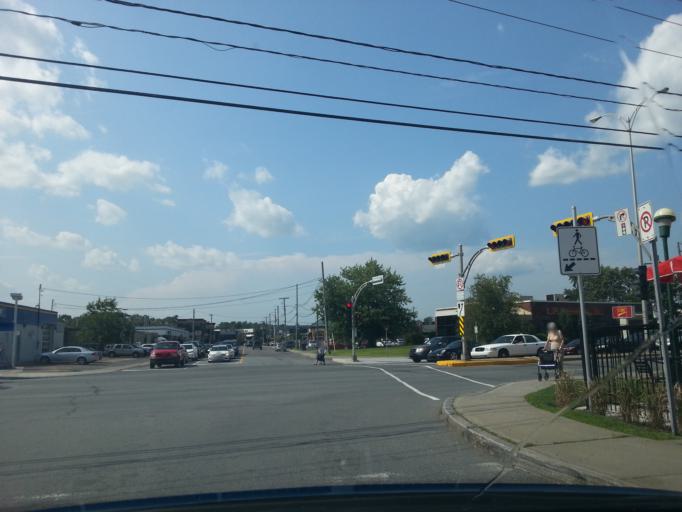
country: CA
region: Quebec
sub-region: Monteregie
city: Beloeil
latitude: 45.5630
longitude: -73.2058
